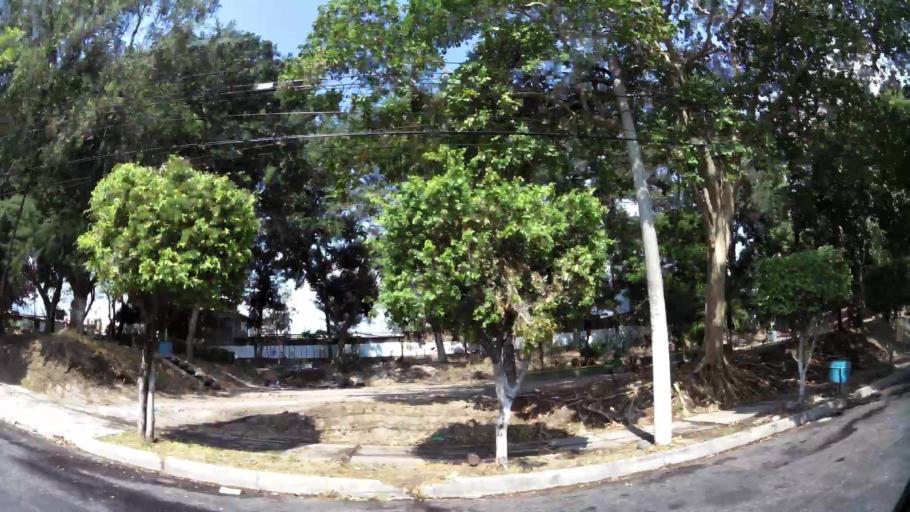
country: SV
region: San Salvador
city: Mejicanos
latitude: 13.7127
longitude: -89.2099
